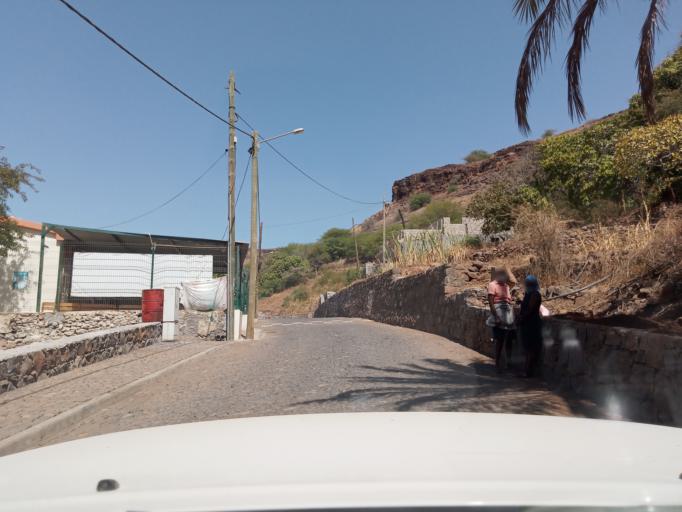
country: CV
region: Ribeira Grande de Santiago
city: Cidade Velha
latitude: 14.9159
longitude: -23.6072
